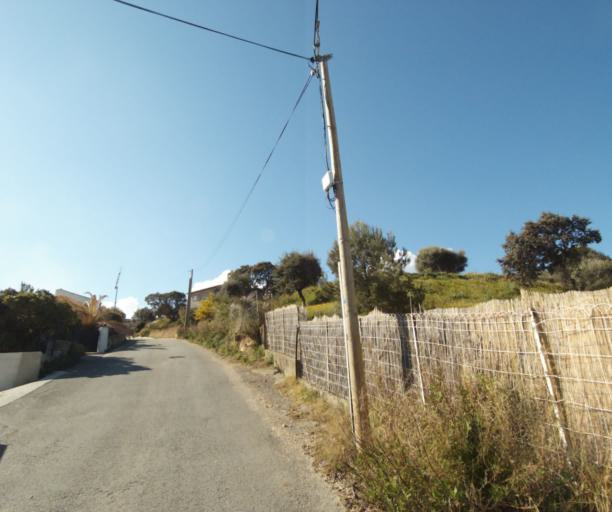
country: FR
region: Corsica
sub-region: Departement de la Corse-du-Sud
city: Propriano
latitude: 41.6699
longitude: 8.9062
